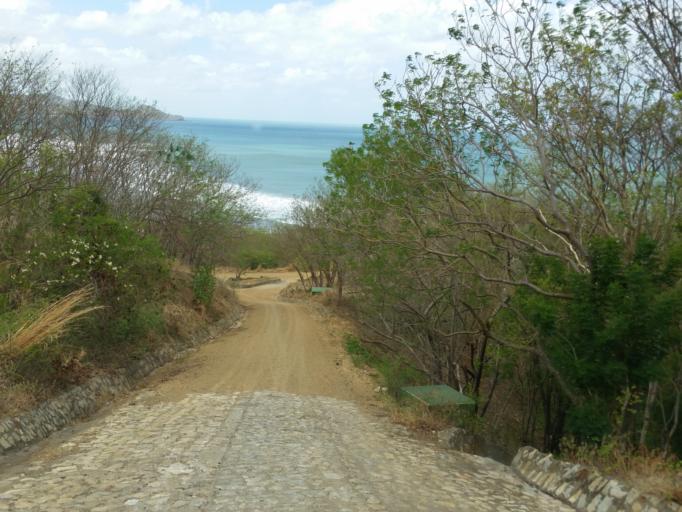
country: NI
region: Rivas
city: Tola
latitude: 11.4152
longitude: -86.0639
